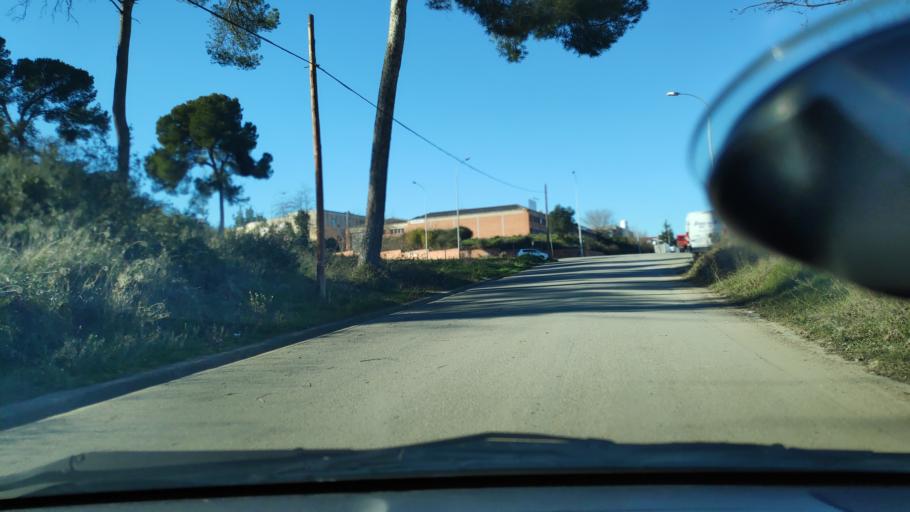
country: ES
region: Catalonia
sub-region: Provincia de Barcelona
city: Sant Quirze del Valles
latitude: 41.5195
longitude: 2.0951
